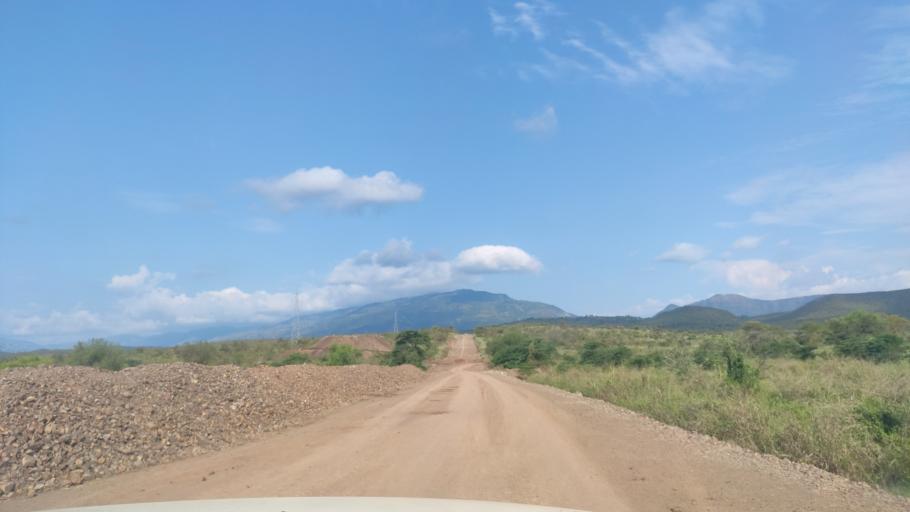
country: ET
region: Southern Nations, Nationalities, and People's Region
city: Felege Neway
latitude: 6.4343
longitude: 37.2690
